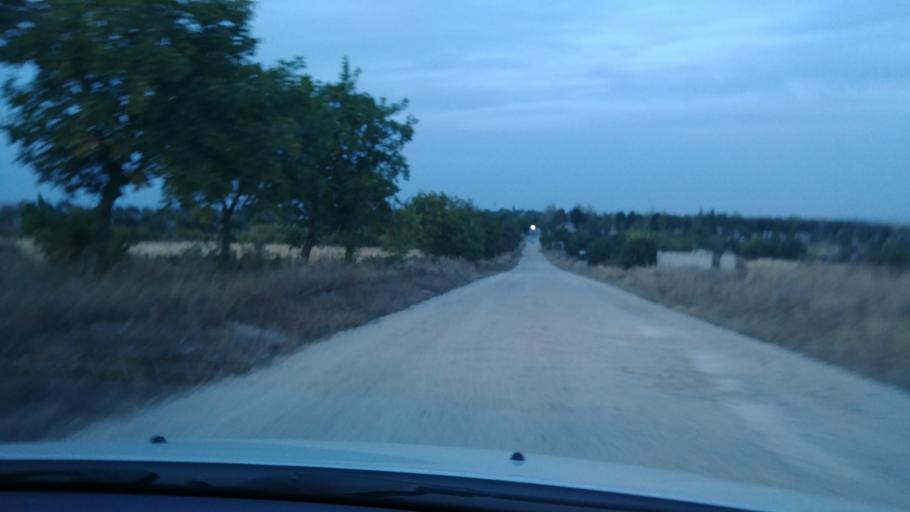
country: MD
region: Rezina
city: Saharna
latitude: 47.6705
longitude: 28.9488
